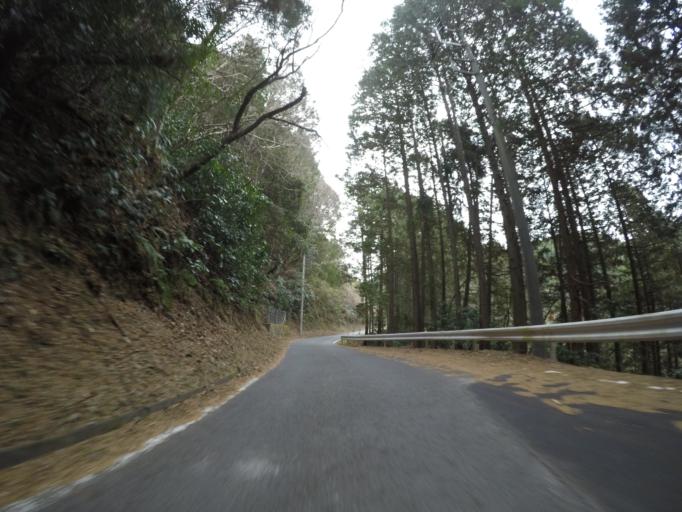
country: JP
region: Shizuoka
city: Fujinomiya
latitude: 35.2559
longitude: 138.5380
